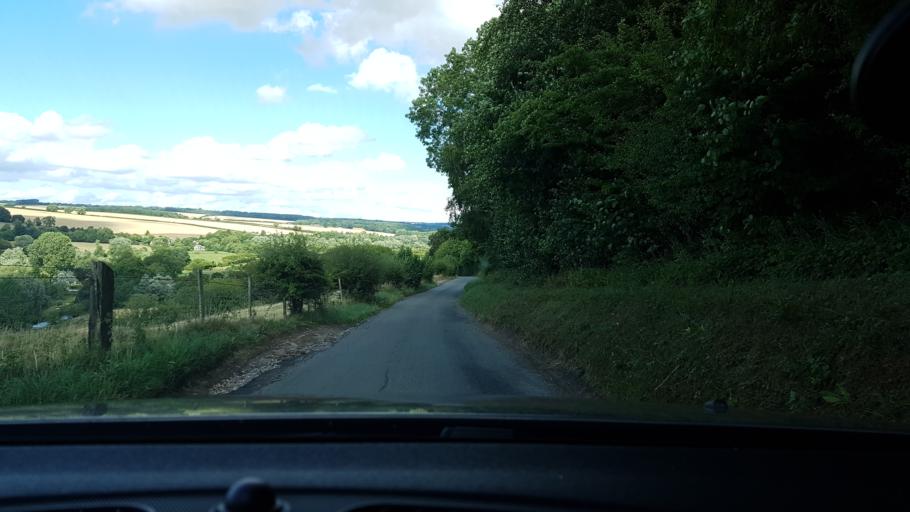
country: GB
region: England
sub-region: Wiltshire
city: Mildenhall
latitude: 51.4207
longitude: -1.6786
